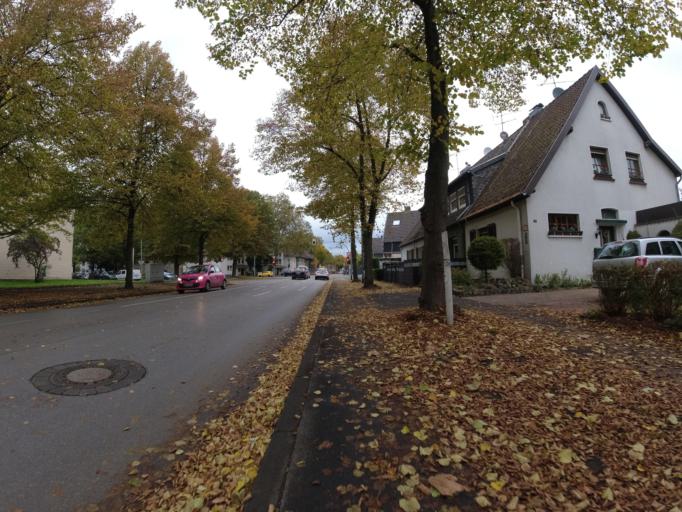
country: DE
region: North Rhine-Westphalia
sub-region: Regierungsbezirk Dusseldorf
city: Hochfeld
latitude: 51.4060
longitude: 6.7202
